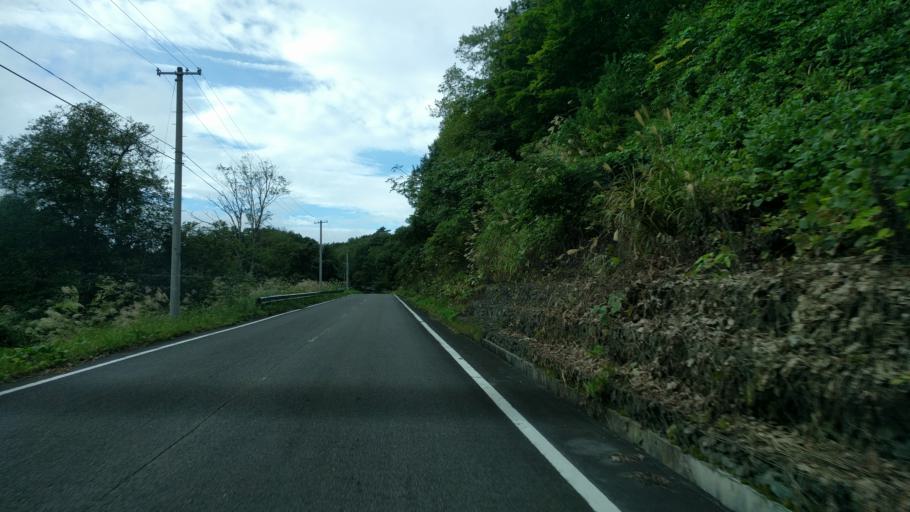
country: JP
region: Fukushima
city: Kitakata
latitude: 37.5133
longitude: 139.7607
